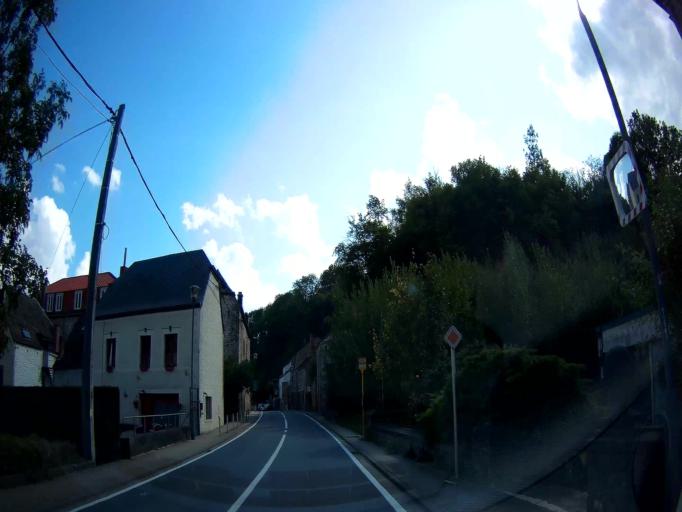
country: BE
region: Wallonia
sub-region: Province de Namur
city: Profondeville
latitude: 50.3473
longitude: 4.8524
